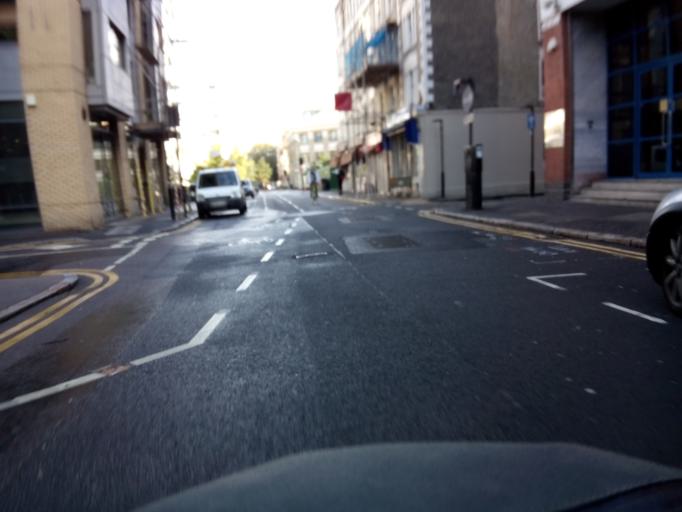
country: GB
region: England
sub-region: Greater London
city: Barbican
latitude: 51.5236
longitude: -0.0844
